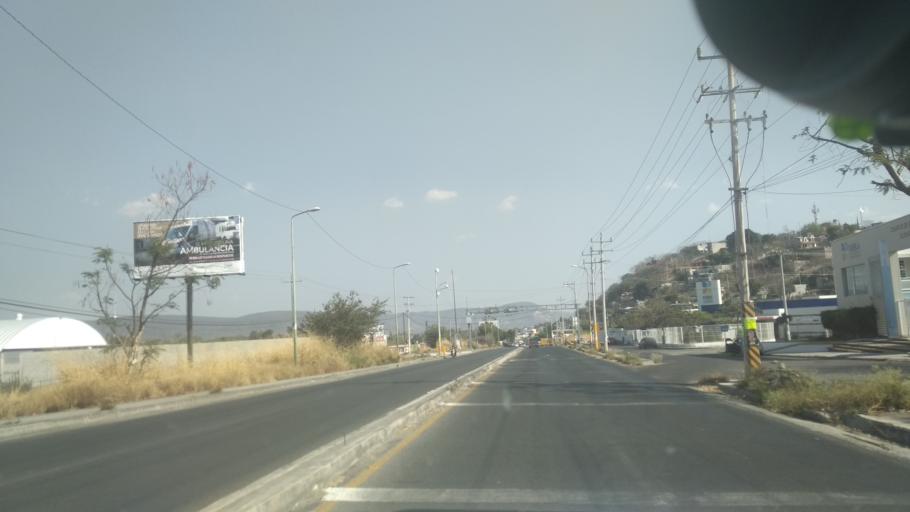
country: MX
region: Puebla
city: Izucar de Matamoros
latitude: 18.6175
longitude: -98.4691
